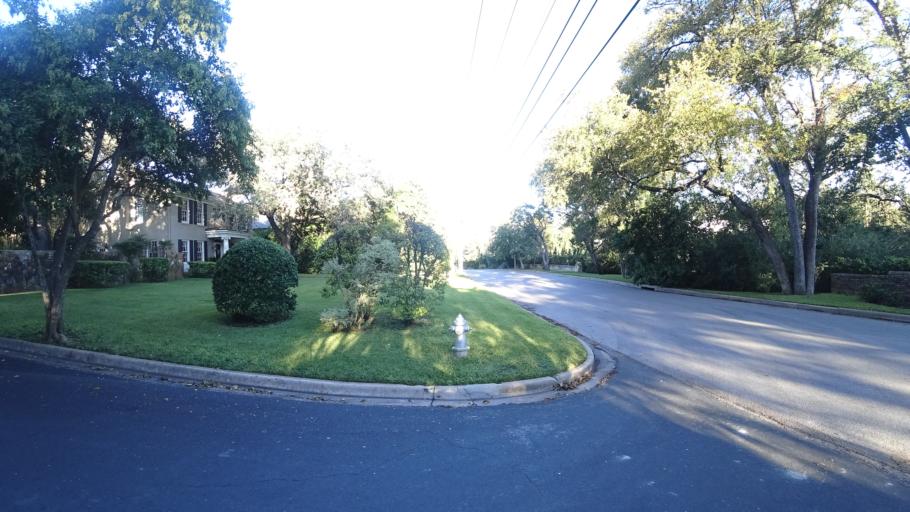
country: US
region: Texas
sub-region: Travis County
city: Rollingwood
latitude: 30.2997
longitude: -97.7715
